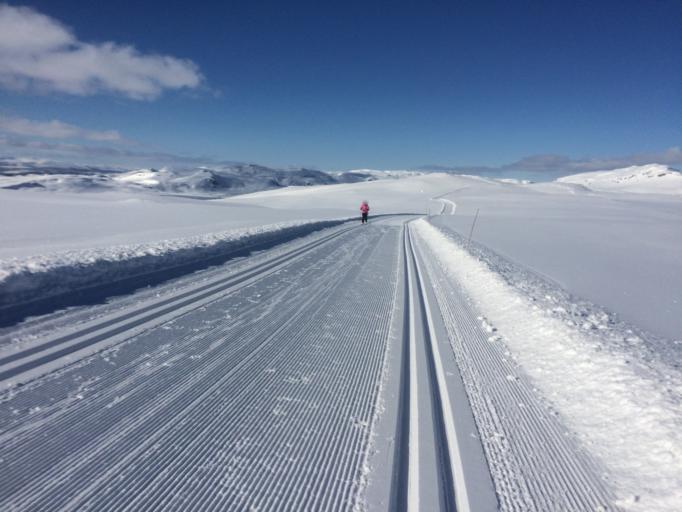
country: NO
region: Oppland
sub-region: Ringebu
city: Ringebu
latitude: 61.3567
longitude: 10.0864
